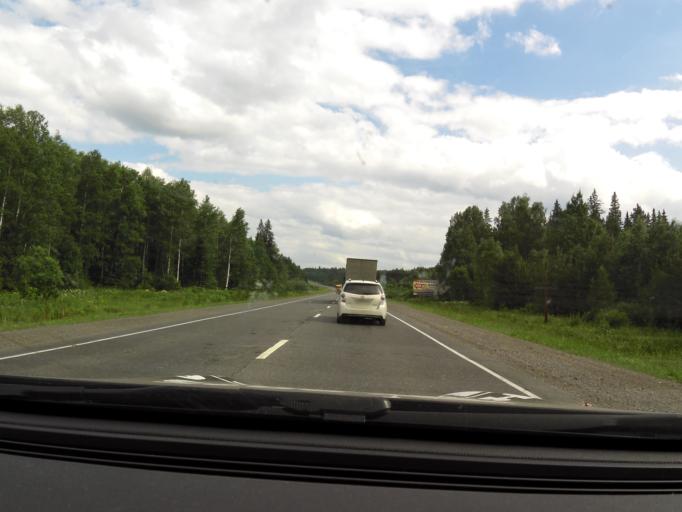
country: RU
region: Sverdlovsk
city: Atig
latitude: 56.8073
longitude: 59.3695
